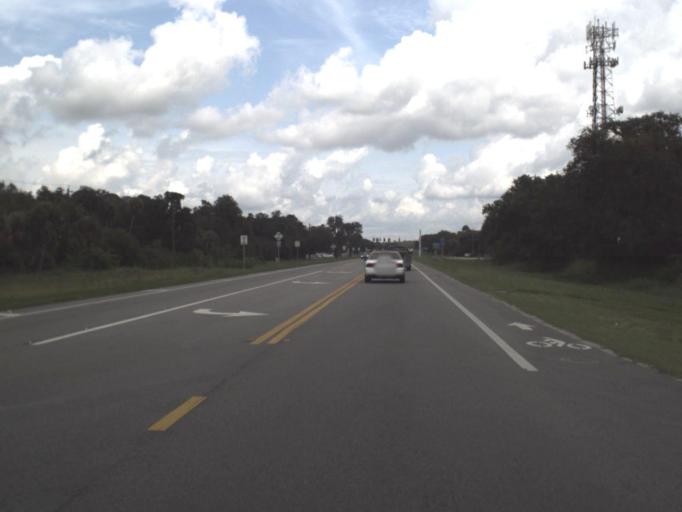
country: US
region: Florida
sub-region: Hendry County
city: LaBelle
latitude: 26.7726
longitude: -81.4374
